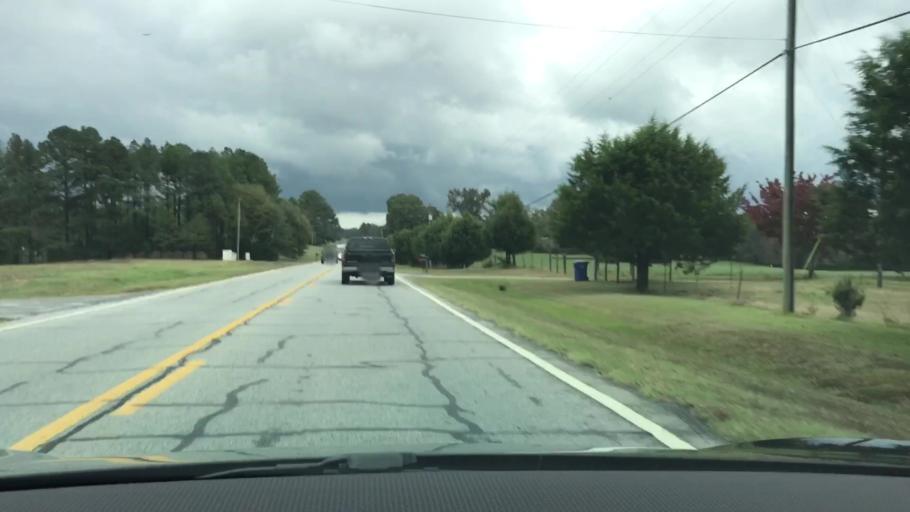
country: US
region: Georgia
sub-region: Oconee County
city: Watkinsville
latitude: 33.7984
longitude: -83.3341
